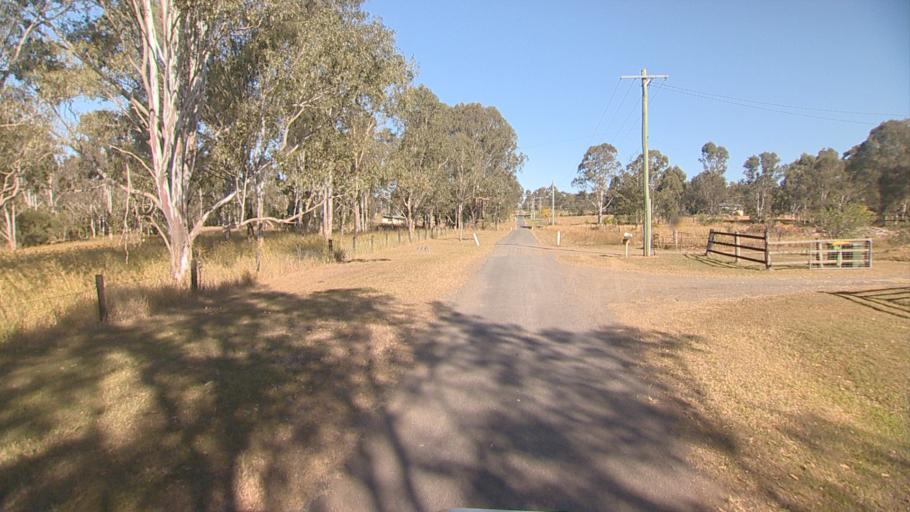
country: AU
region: Queensland
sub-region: Logan
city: North Maclean
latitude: -27.7740
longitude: 153.0253
